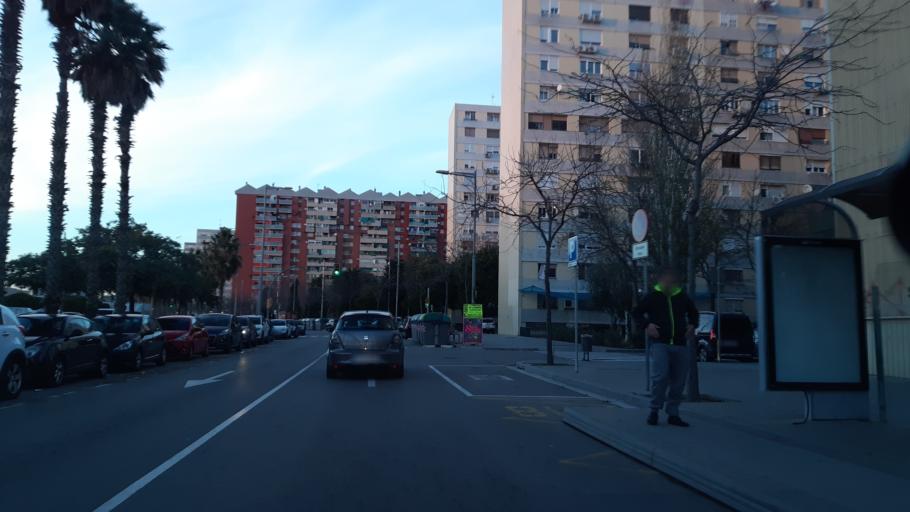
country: ES
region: Catalonia
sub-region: Provincia de Barcelona
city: L'Hospitalet de Llobregat
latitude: 41.3482
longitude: 2.1068
